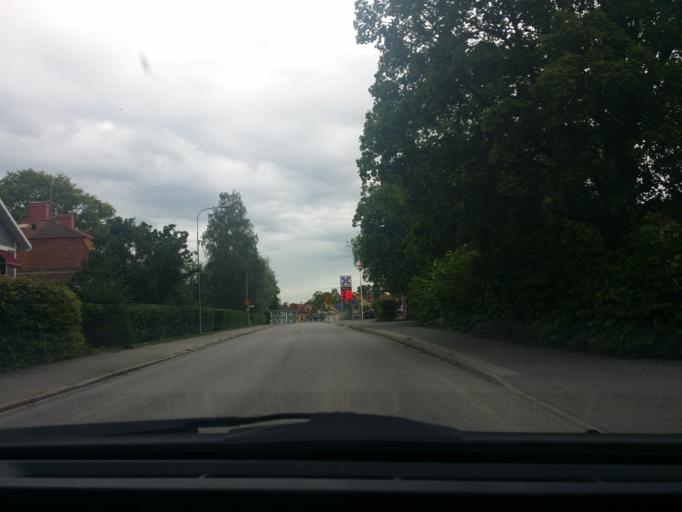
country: SE
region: OErebro
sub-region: Nora Kommun
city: Nora
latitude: 59.5234
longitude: 15.0358
